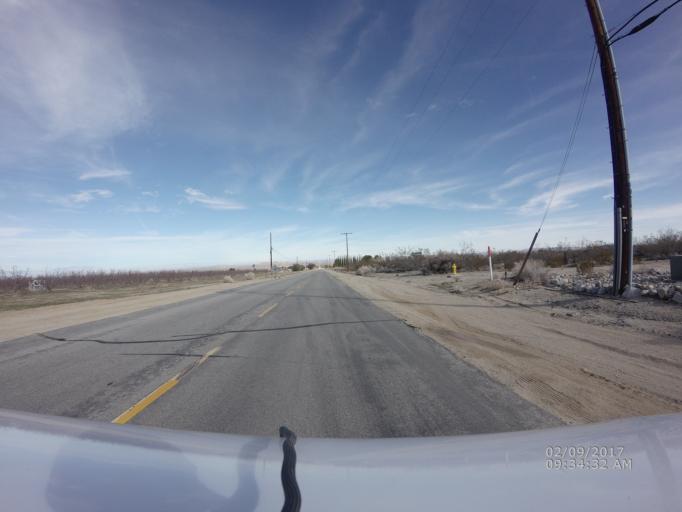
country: US
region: California
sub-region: Los Angeles County
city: Lake Los Angeles
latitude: 34.4862
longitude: -117.8353
